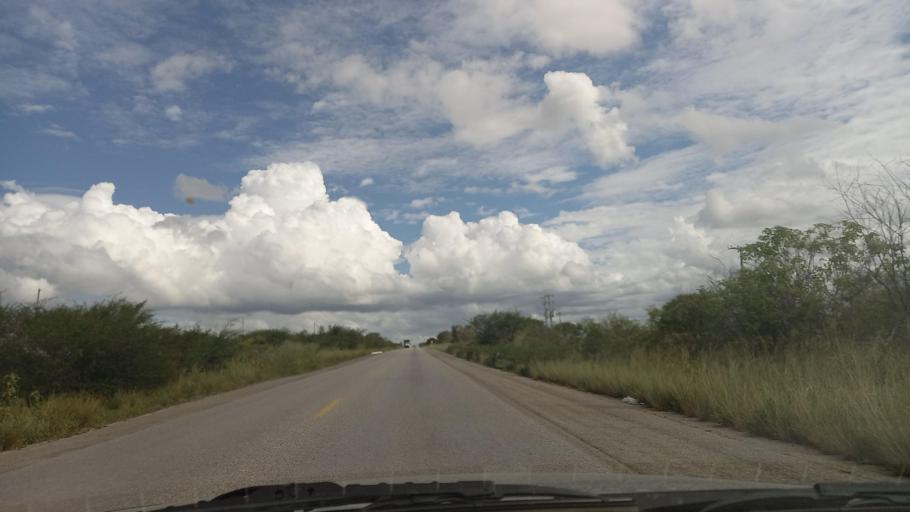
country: BR
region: Pernambuco
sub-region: Cachoeirinha
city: Cachoeirinha
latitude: -8.4388
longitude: -36.2046
